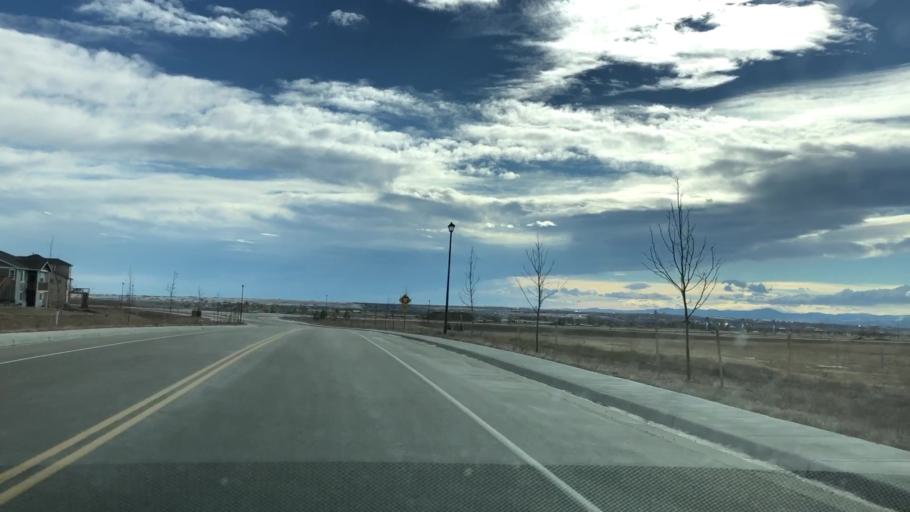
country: US
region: Colorado
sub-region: Weld County
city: Windsor
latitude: 40.5325
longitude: -104.9386
